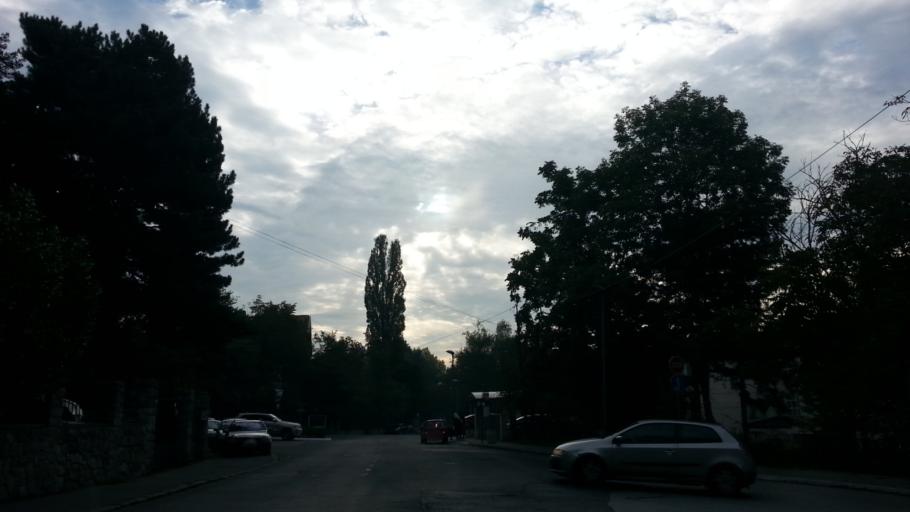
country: RS
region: Central Serbia
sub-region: Belgrade
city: Savski Venac
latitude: 44.7697
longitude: 20.4548
